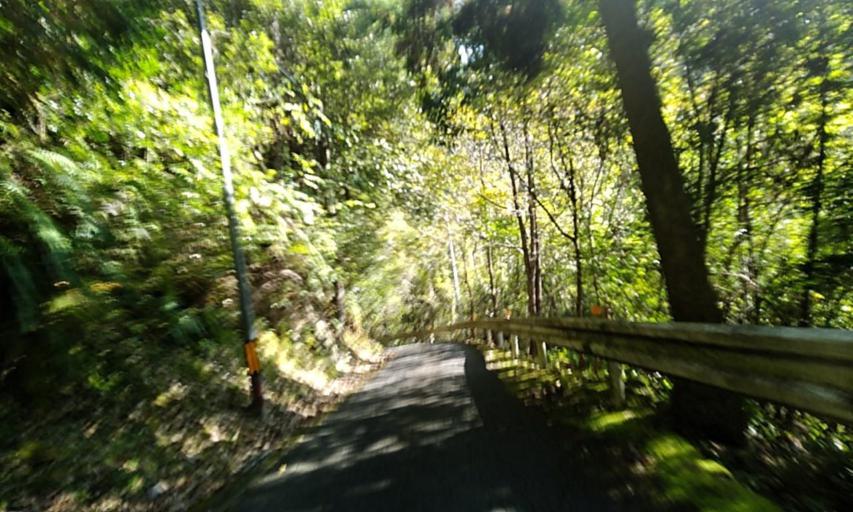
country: JP
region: Wakayama
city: Shingu
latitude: 33.9116
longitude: 135.9883
